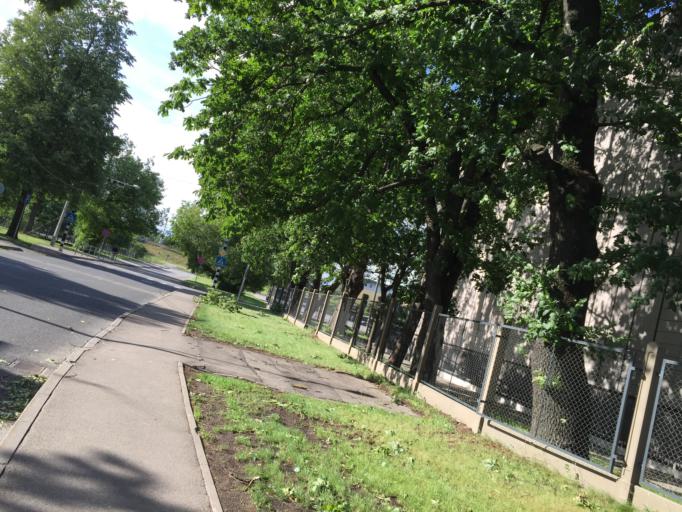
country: LV
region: Riga
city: Riga
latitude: 56.9446
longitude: 24.1302
